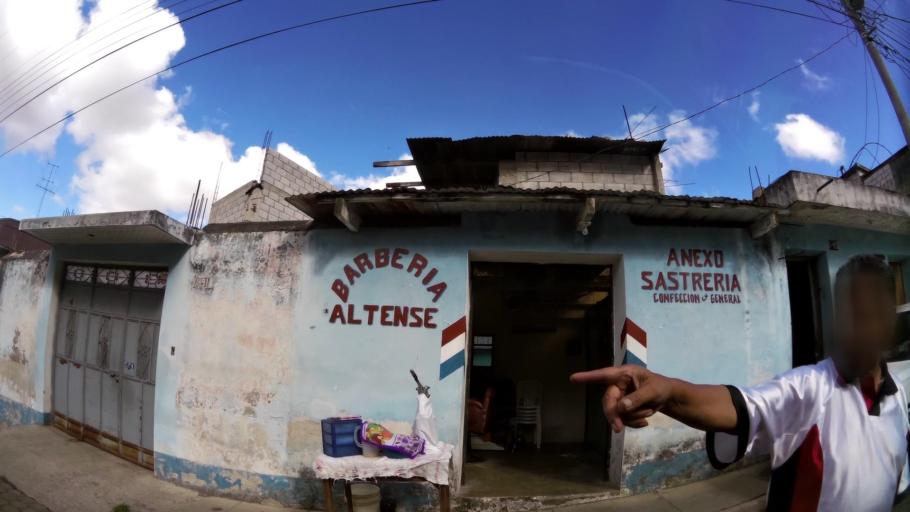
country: GT
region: Quetzaltenango
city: Quetzaltenango
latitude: 14.8342
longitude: -91.5064
